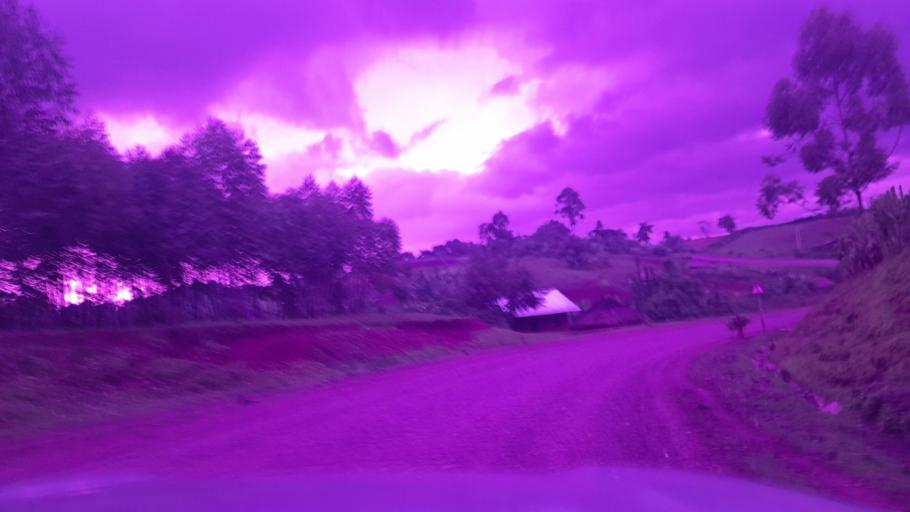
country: ET
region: Southern Nations, Nationalities, and People's Region
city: Mizan Teferi
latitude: 6.8906
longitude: 35.8486
